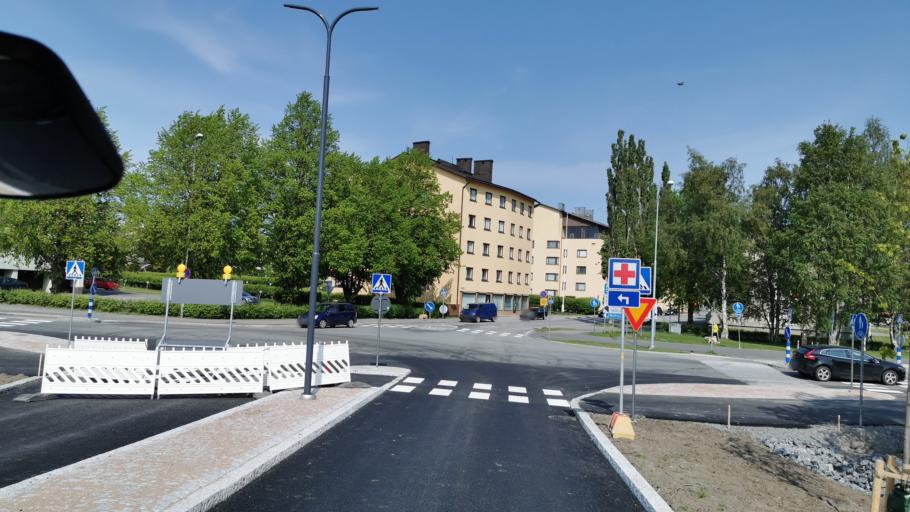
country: FI
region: Ostrobothnia
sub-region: Vaasa
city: Vaasa
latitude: 63.0864
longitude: 21.6264
